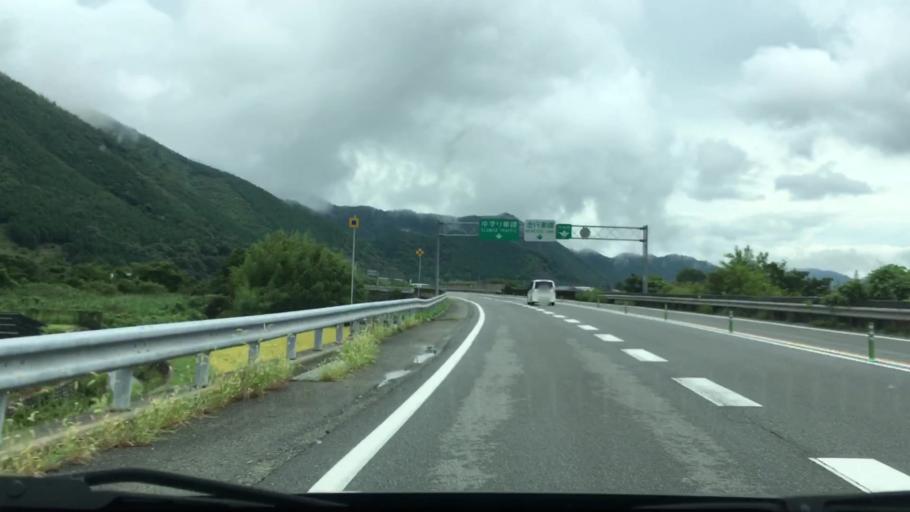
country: JP
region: Hyogo
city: Yamazakicho-nakabirose
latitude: 35.0501
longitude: 134.7640
